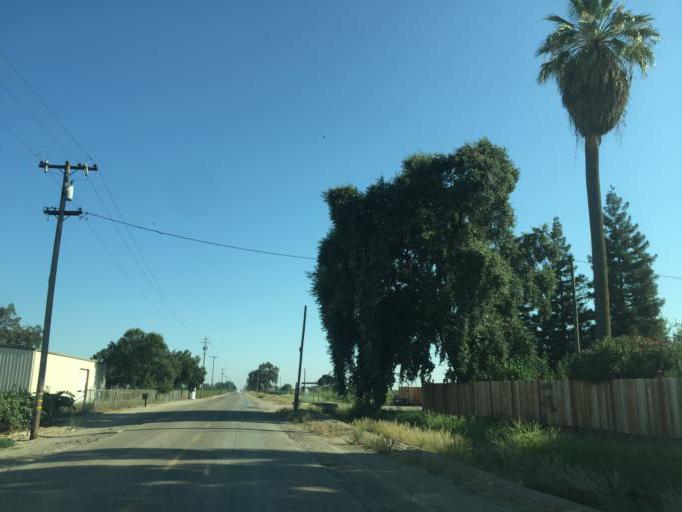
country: US
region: California
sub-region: Fresno County
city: Kingsburg
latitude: 36.4648
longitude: -119.5284
